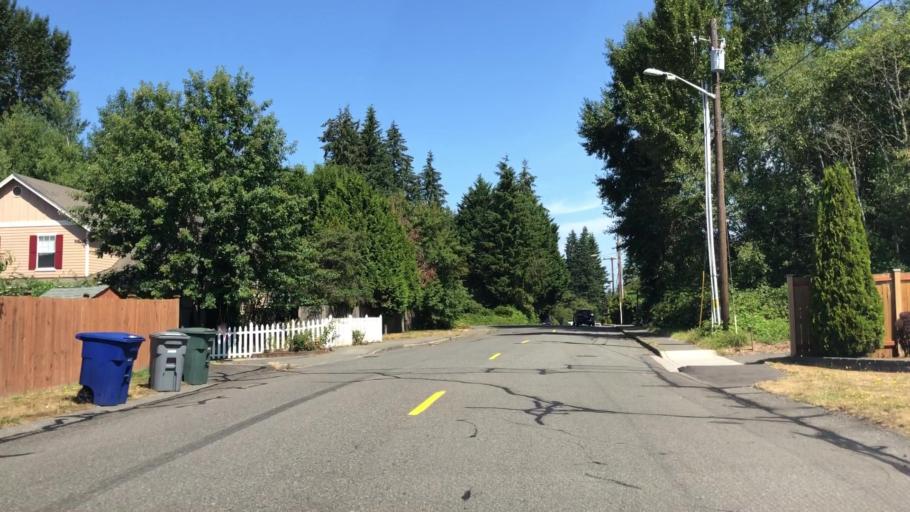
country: US
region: Washington
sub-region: King County
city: Inglewood-Finn Hill
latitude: 47.7353
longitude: -122.2411
